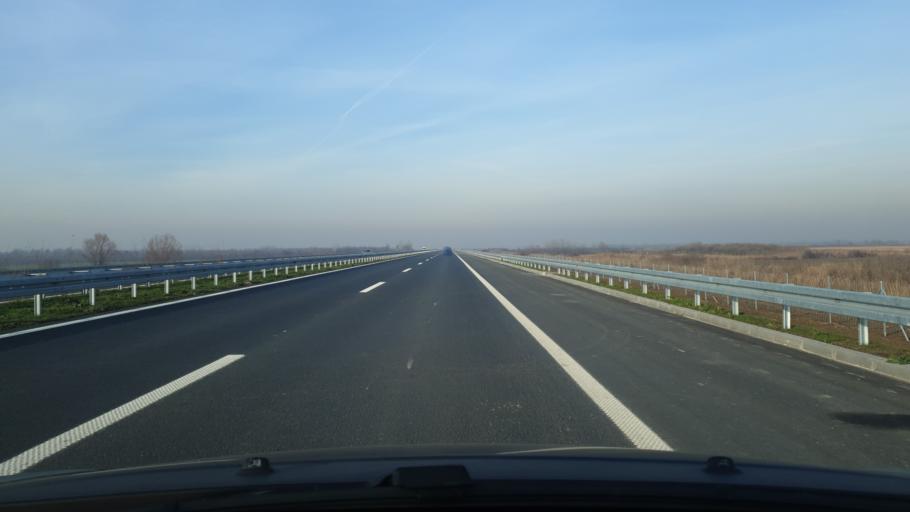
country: RS
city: Umka
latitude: 44.6972
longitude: 20.2654
